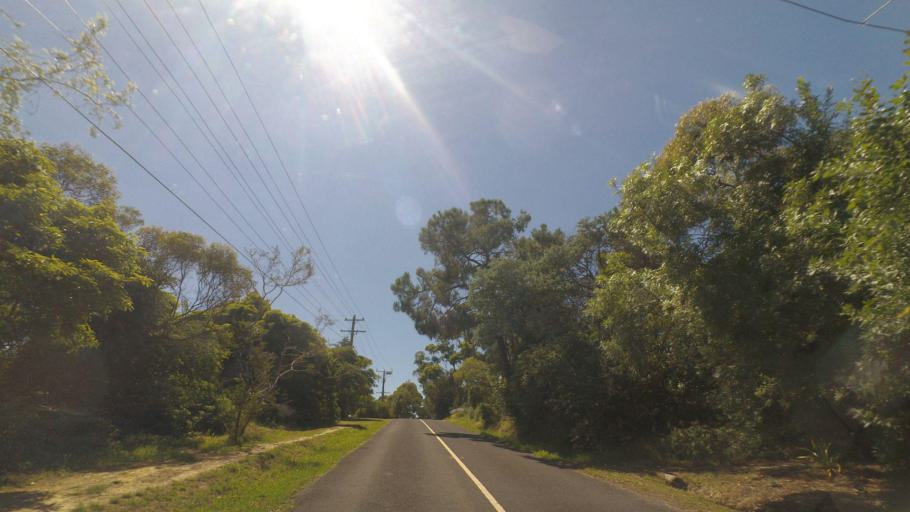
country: AU
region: Victoria
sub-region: Maroondah
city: Warranwood
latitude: -37.7789
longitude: 145.2361
